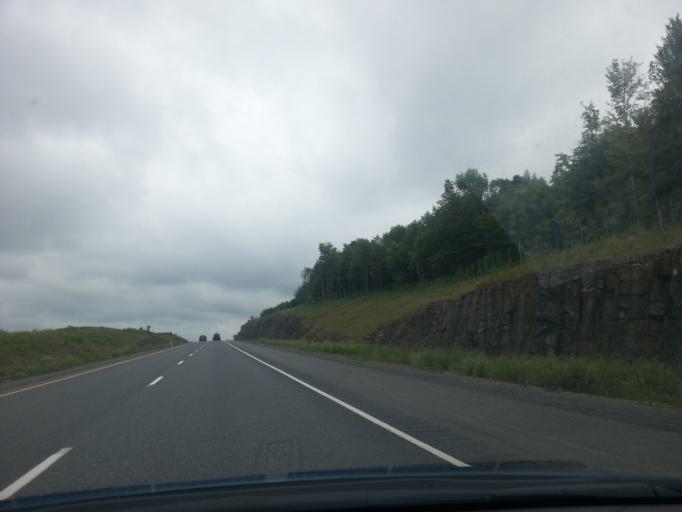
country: CA
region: New Brunswick
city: Florenceville-Bristol
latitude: 46.5025
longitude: -67.6909
